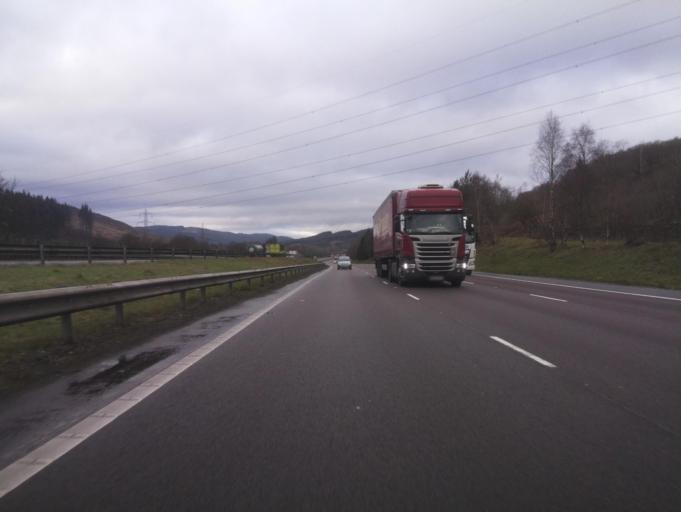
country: GB
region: Scotland
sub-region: Dumfries and Galloway
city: Moffat
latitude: 55.3302
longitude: -3.4757
